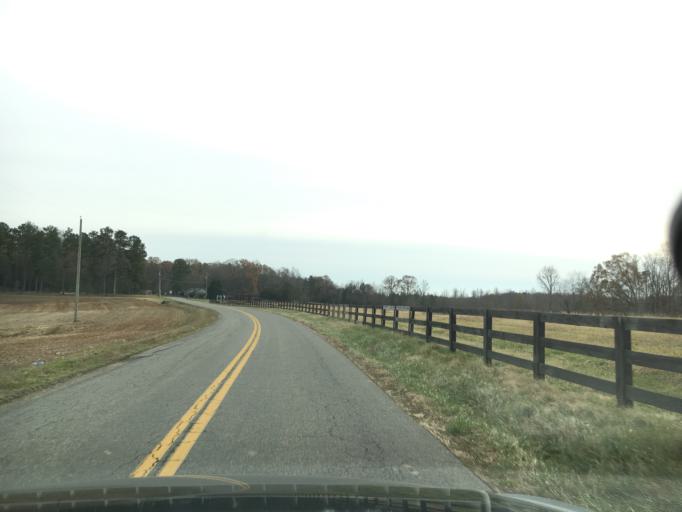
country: US
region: Virginia
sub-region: Henrico County
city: Wyndham
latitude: 37.7121
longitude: -77.6840
